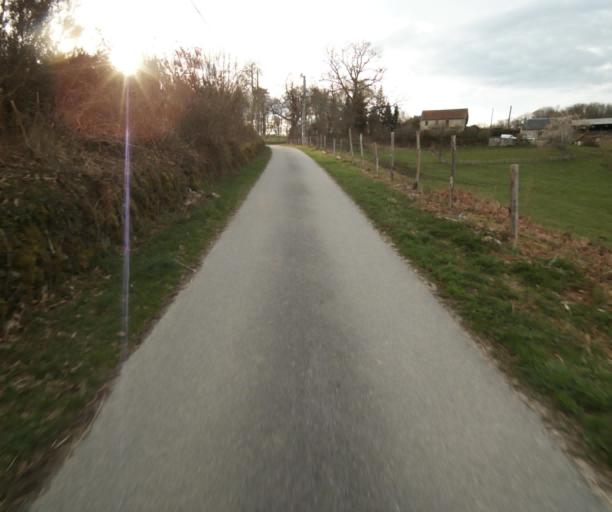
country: FR
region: Limousin
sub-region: Departement de la Correze
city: Argentat
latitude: 45.2277
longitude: 1.9520
